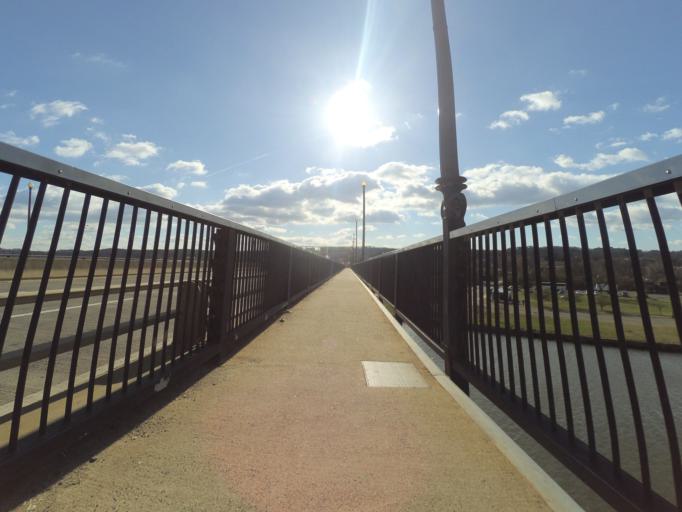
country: US
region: Maryland
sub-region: Prince George's County
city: Silver Hill
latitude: 38.8766
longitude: -76.9777
